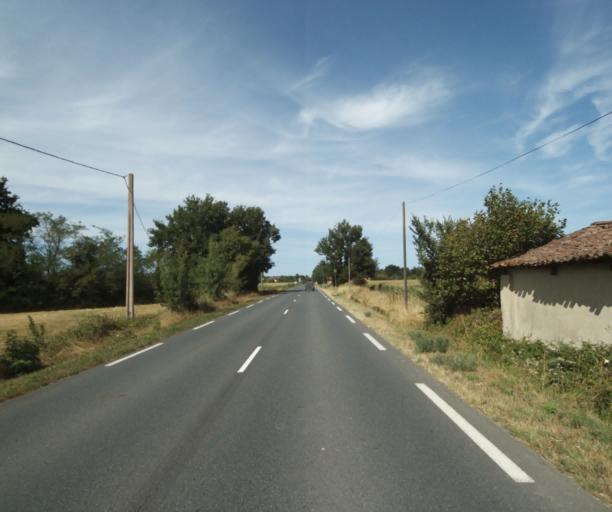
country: FR
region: Midi-Pyrenees
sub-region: Departement du Tarn
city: Soreze
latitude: 43.5149
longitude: 2.0671
